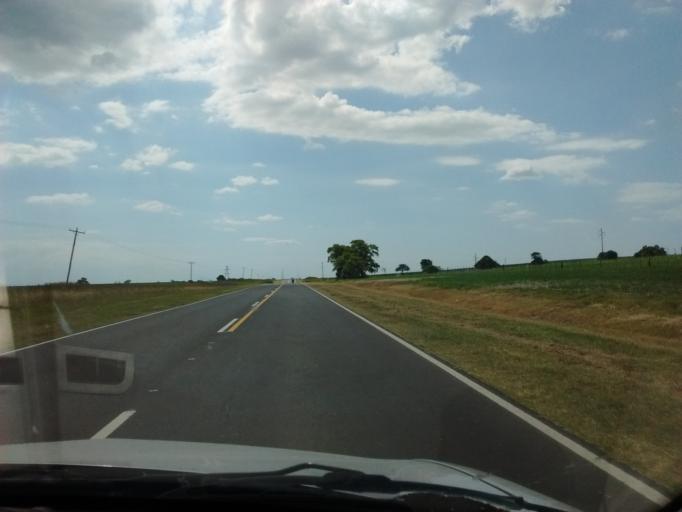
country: AR
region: Entre Rios
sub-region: Departamento de Victoria
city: Victoria
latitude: -32.6645
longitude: -60.0460
